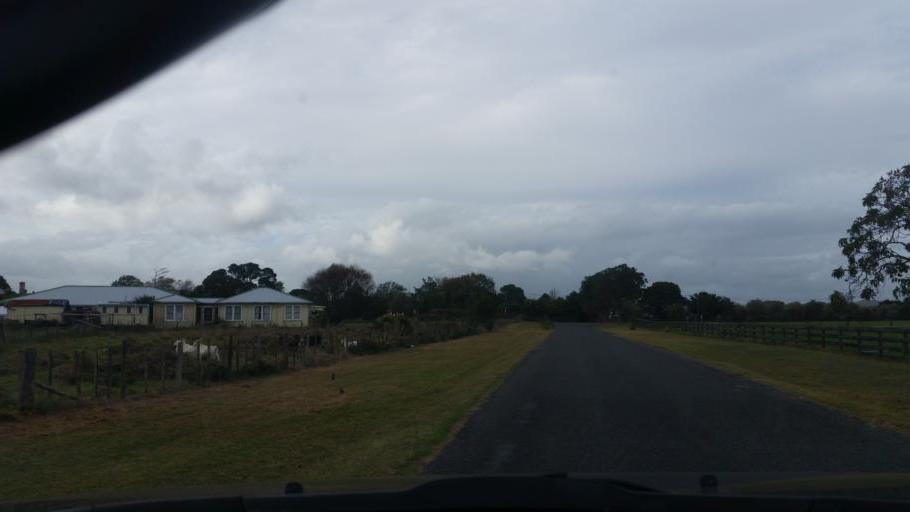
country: NZ
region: Northland
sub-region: Kaipara District
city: Dargaville
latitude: -36.0275
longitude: 173.9151
